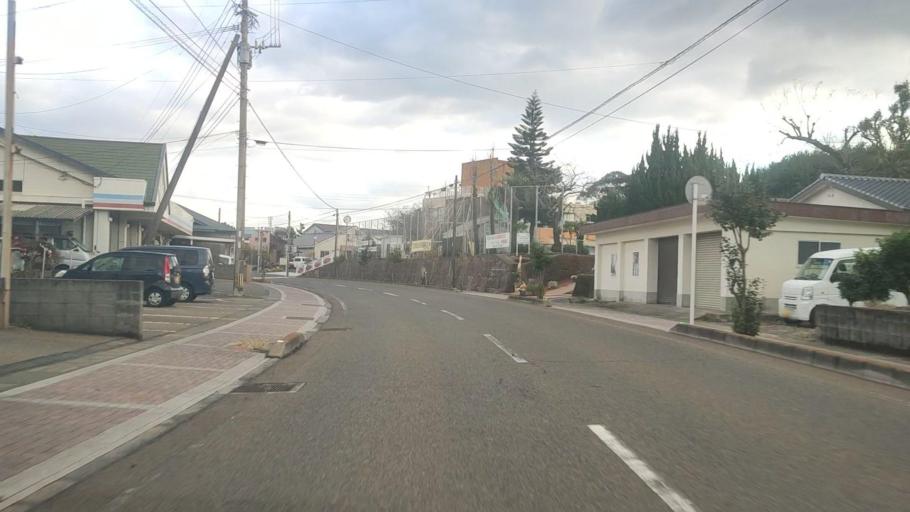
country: JP
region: Kagoshima
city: Kagoshima-shi
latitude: 31.5972
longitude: 130.6074
